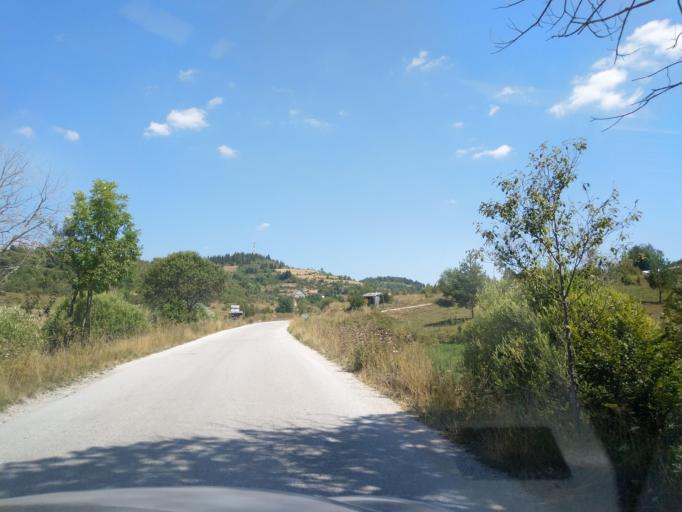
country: RS
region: Central Serbia
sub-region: Zlatiborski Okrug
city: Nova Varos
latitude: 43.4505
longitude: 19.9676
